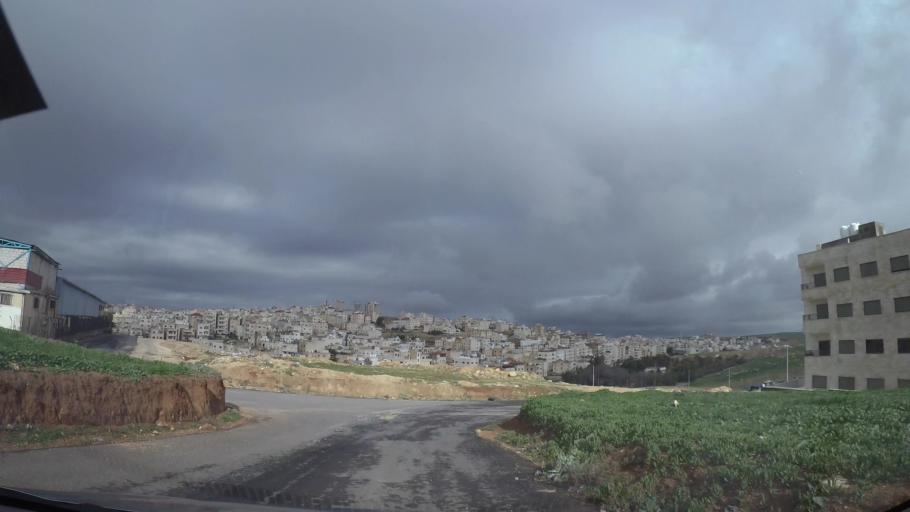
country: JO
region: Amman
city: Al Jubayhah
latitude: 32.0625
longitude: 35.8871
